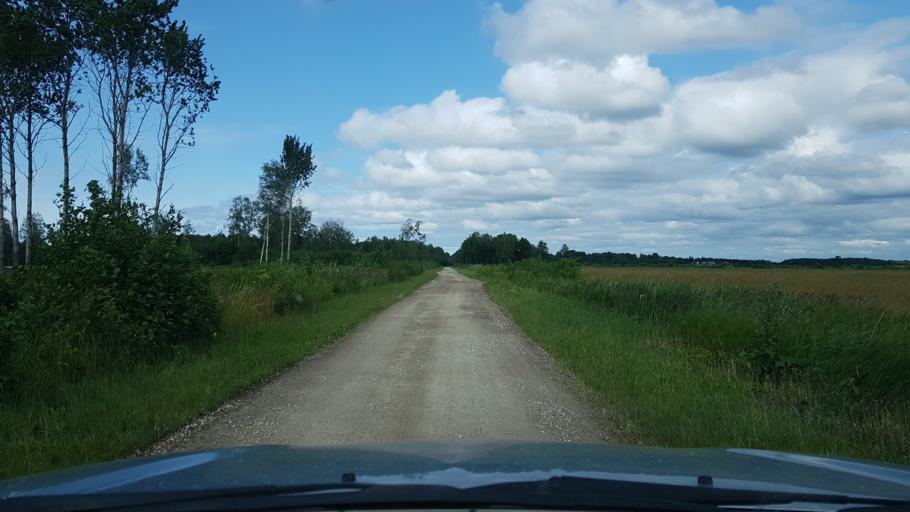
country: EE
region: Ida-Virumaa
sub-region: Narva-Joesuu linn
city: Narva-Joesuu
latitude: 59.3661
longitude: 27.9244
